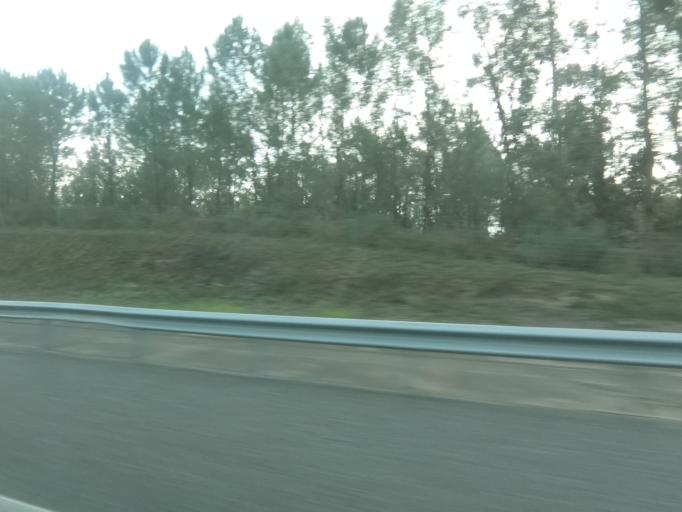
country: ES
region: Galicia
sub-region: Provincia de Pontevedra
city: Tui
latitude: 42.0800
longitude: -8.6396
